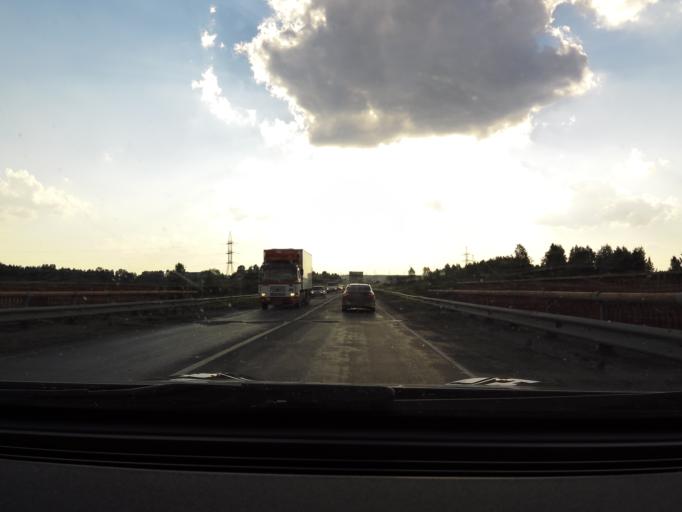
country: RU
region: Sverdlovsk
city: Revda
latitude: 56.8266
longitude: 59.9680
